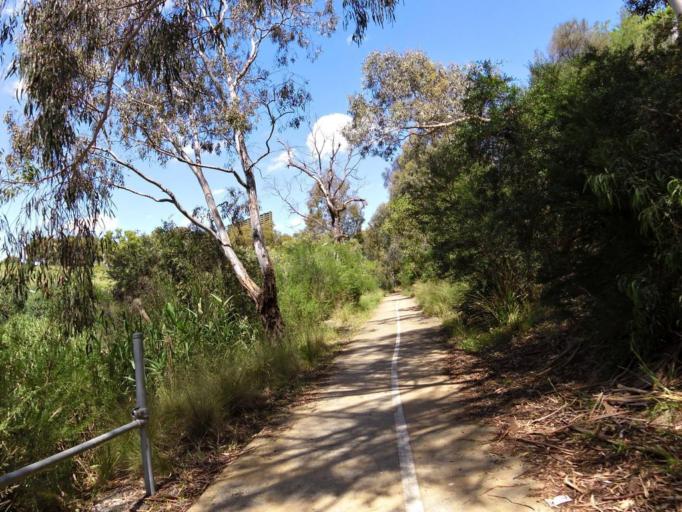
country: AU
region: Victoria
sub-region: Moreland
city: Fawkner
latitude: -37.7202
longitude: 144.9725
